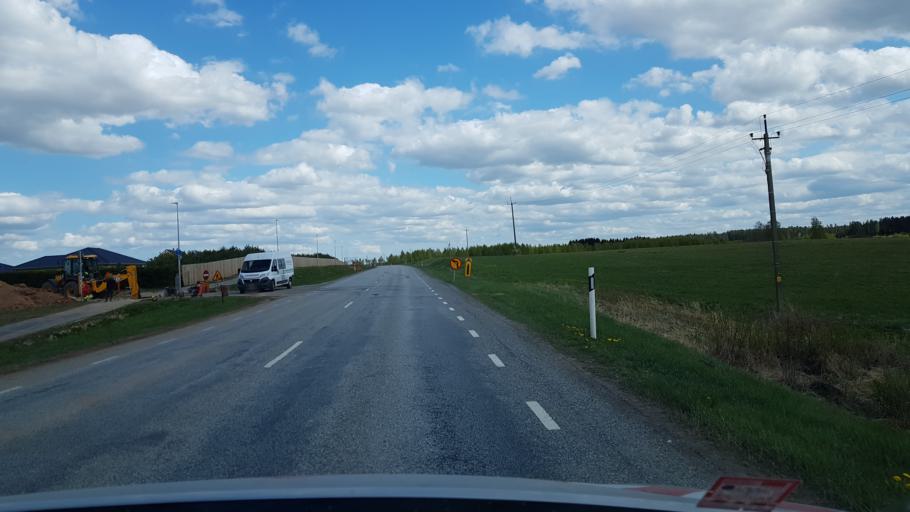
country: EE
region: Tartu
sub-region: UElenurme vald
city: Ulenurme
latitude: 58.3248
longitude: 26.7919
